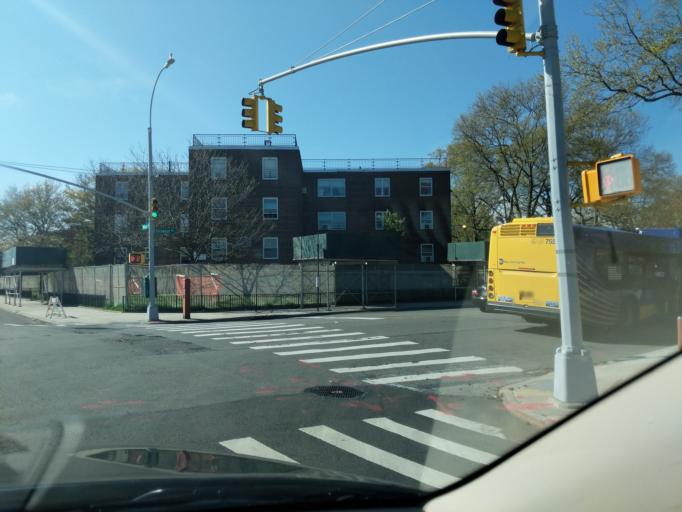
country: US
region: New York
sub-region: Kings County
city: East New York
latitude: 40.6515
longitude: -73.8929
